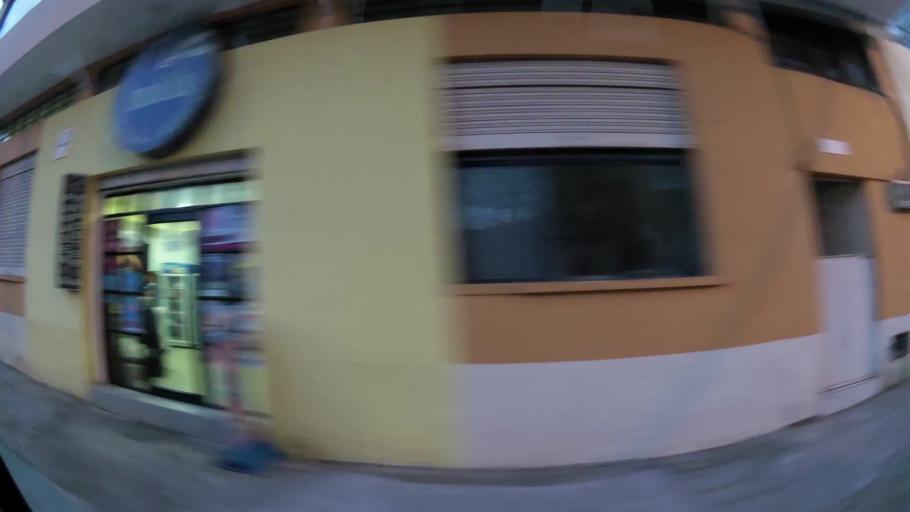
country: EC
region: Tungurahua
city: Ambato
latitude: -1.2505
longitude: -78.6384
